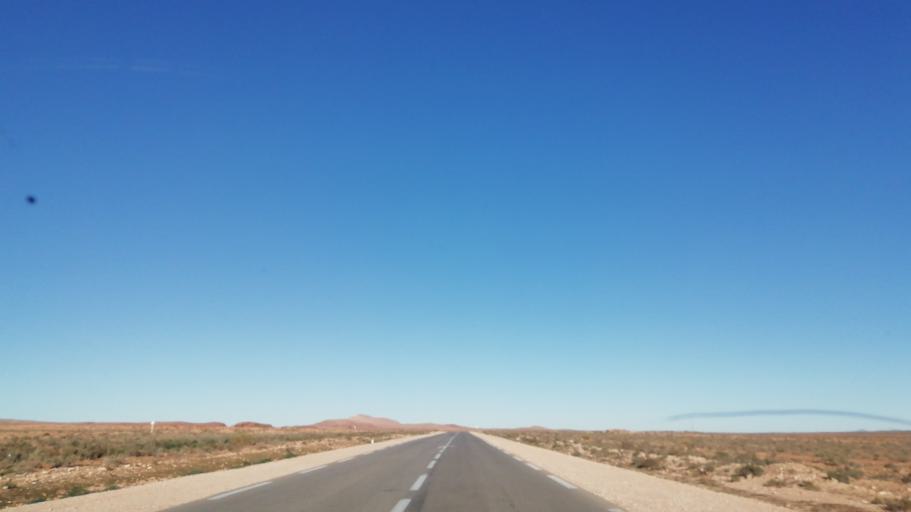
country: DZ
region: El Bayadh
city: El Abiodh Sidi Cheikh
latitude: 33.1042
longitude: 0.2142
